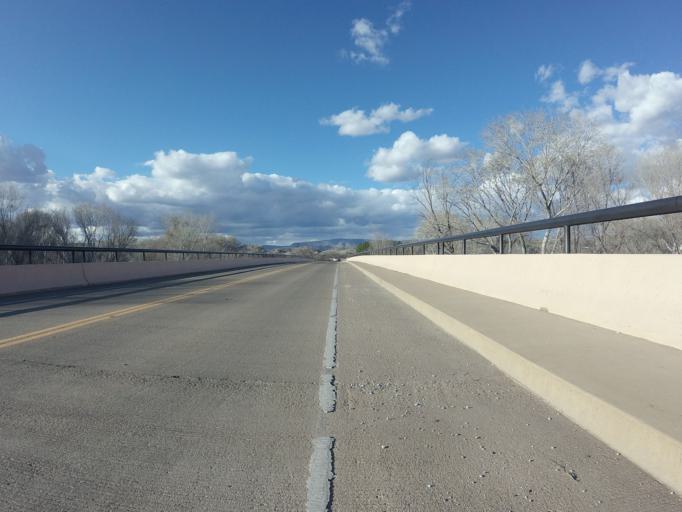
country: US
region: Arizona
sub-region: Yavapai County
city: Cottonwood
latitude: 34.7500
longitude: -112.0220
